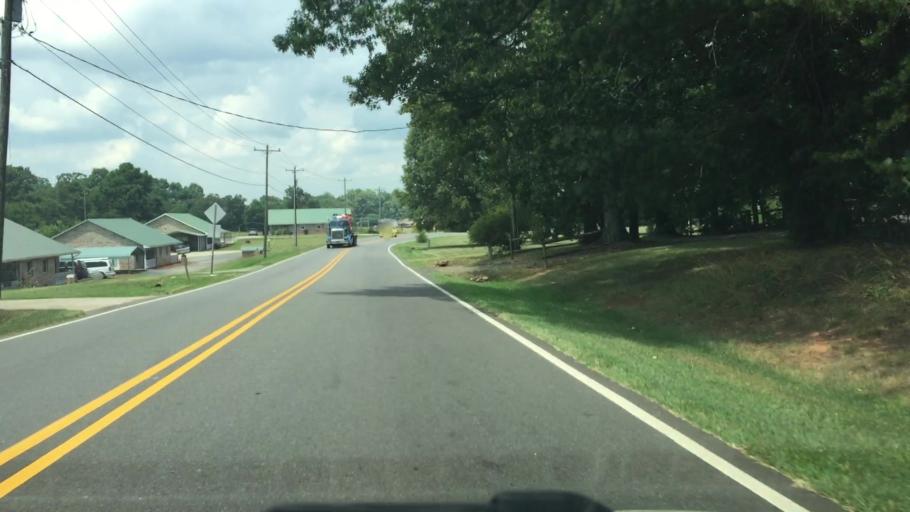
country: US
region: North Carolina
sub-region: Iredell County
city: Troutman
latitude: 35.7209
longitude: -80.8737
